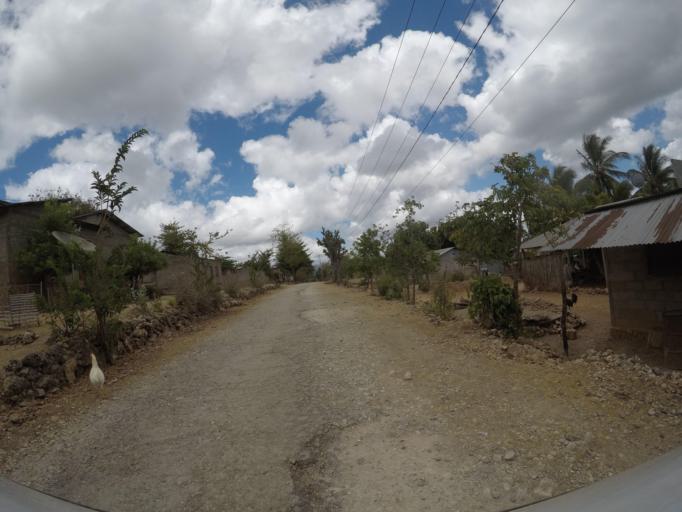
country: TL
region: Lautem
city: Lospalos
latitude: -8.3827
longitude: 126.9204
